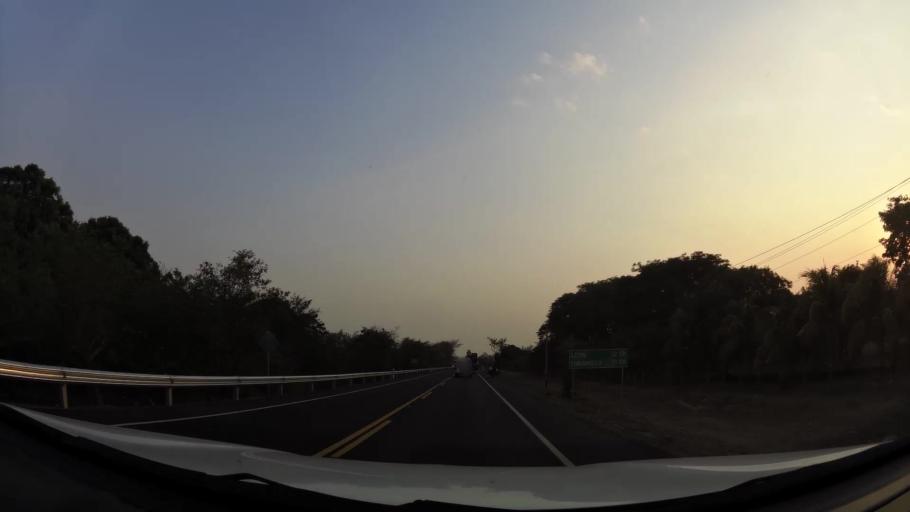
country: NI
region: Leon
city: La Paz Centro
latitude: 12.3301
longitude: -86.6842
